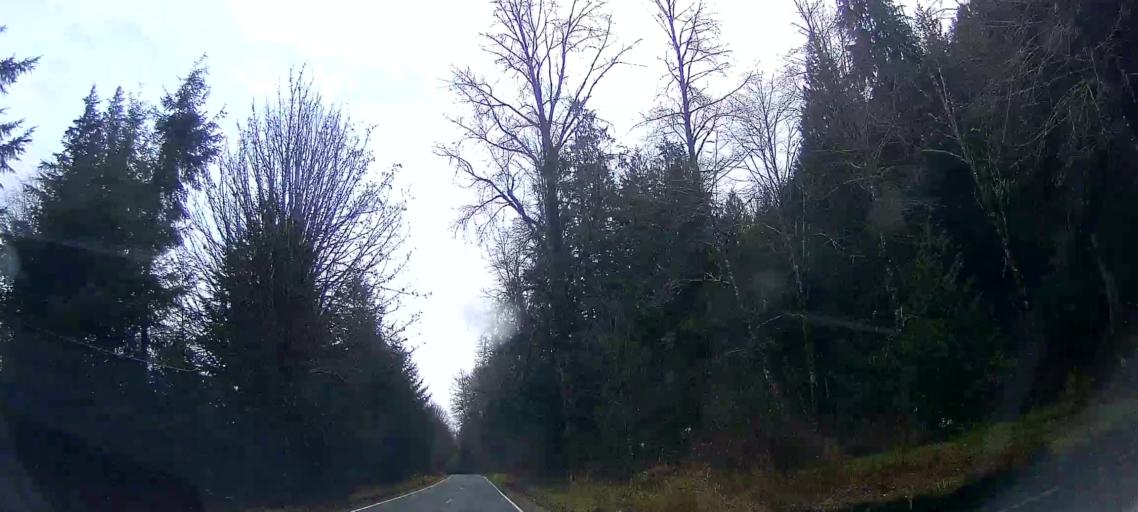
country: US
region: Washington
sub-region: Skagit County
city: Sedro-Woolley
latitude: 48.5131
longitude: -121.9388
